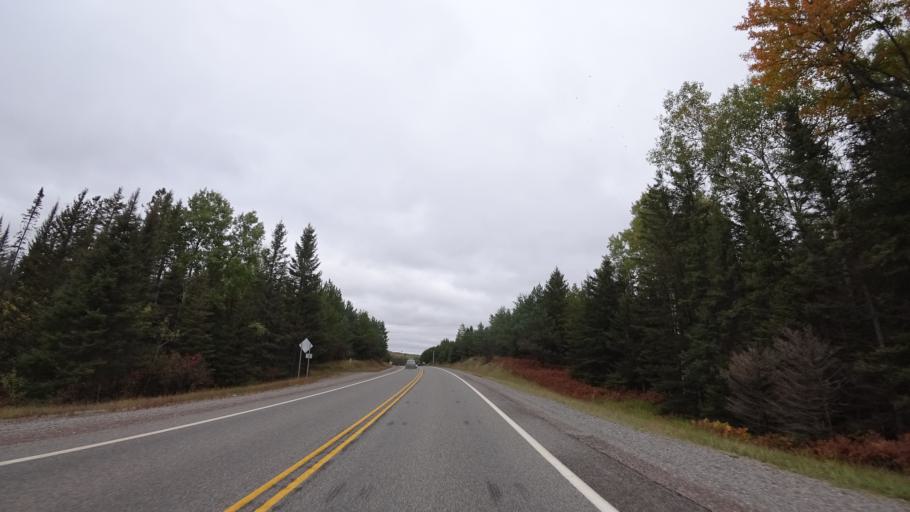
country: US
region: Michigan
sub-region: Marquette County
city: West Ishpeming
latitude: 46.4924
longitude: -87.9191
